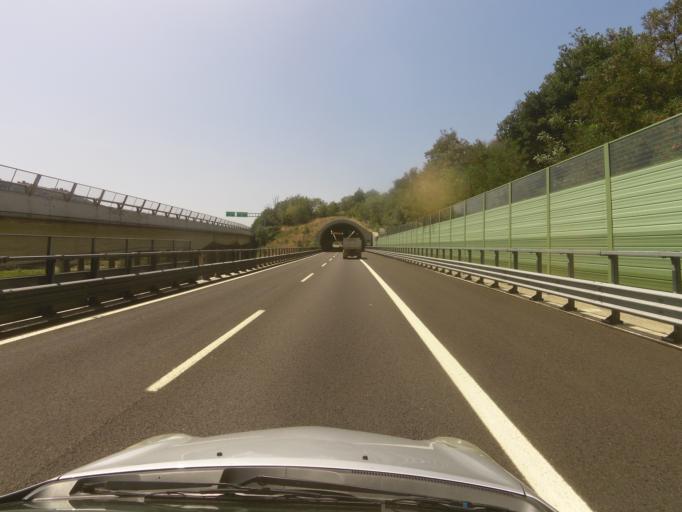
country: IT
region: Emilia-Romagna
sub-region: Provincia di Bologna
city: Marzabotto
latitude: 44.2914
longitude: 11.2089
